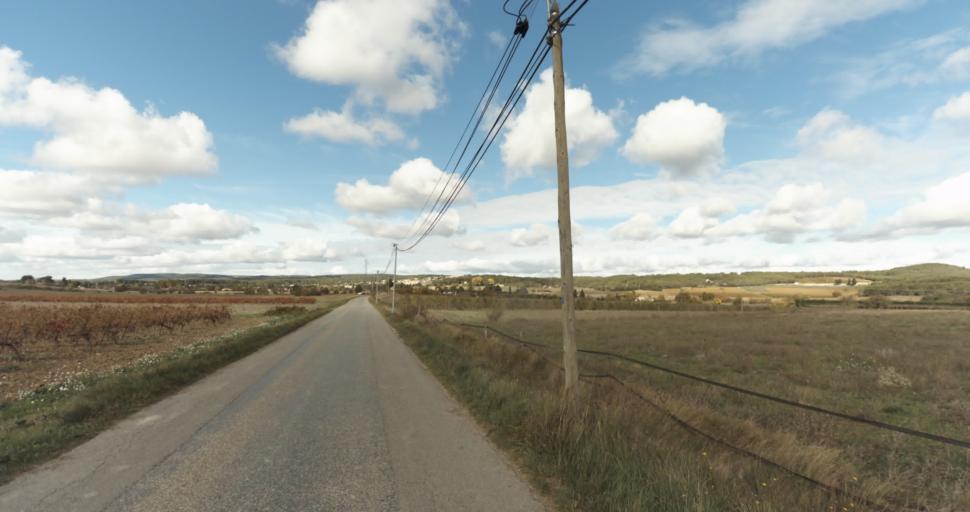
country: FR
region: Provence-Alpes-Cote d'Azur
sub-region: Departement des Bouches-du-Rhone
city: Venelles
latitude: 43.5807
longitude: 5.4958
